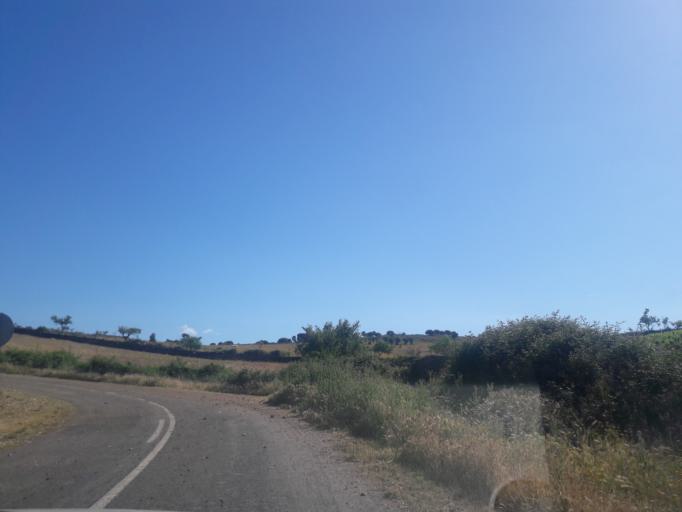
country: ES
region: Castille and Leon
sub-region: Provincia de Salamanca
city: Saucelle
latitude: 41.0400
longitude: -6.7598
